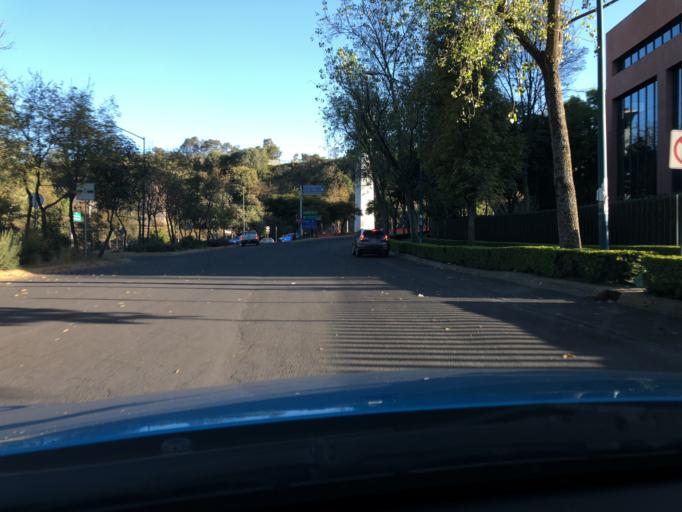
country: MX
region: Mexico City
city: Col. Bosques de las Lomas
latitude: 19.3736
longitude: -99.2599
